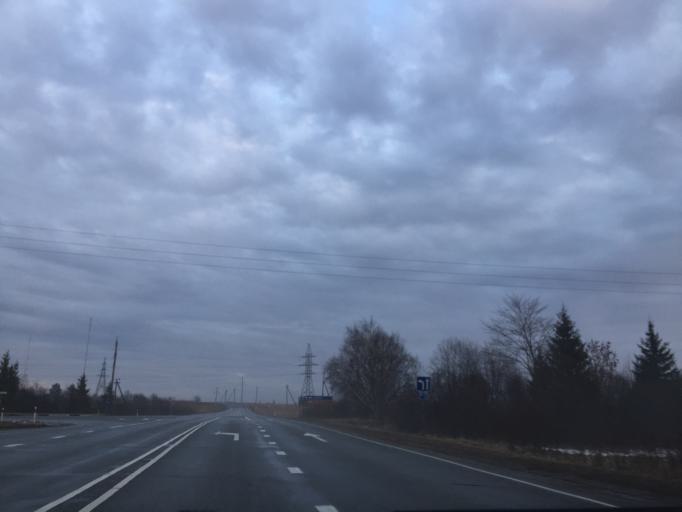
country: EE
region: Laeaene
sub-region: Lihula vald
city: Lihula
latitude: 58.6811
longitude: 23.8134
